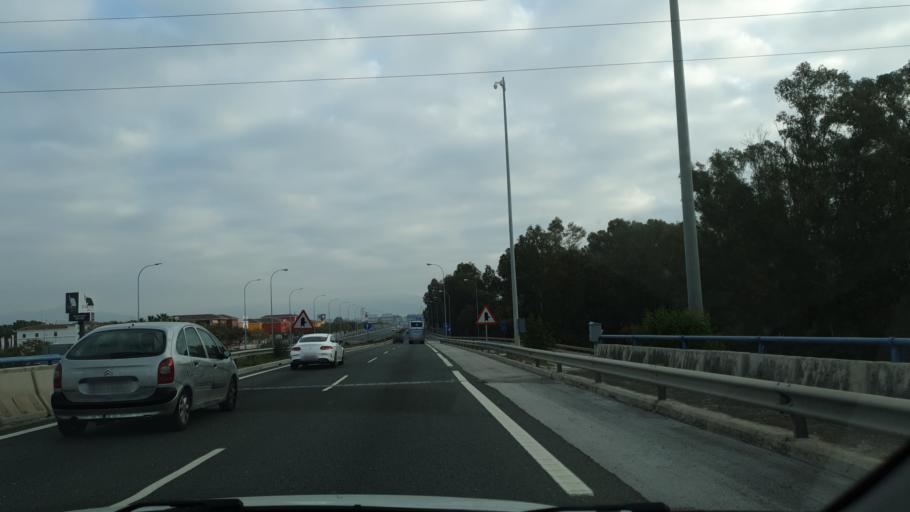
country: ES
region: Andalusia
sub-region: Provincia de Malaga
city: Torremolinos
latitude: 36.6535
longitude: -4.4785
